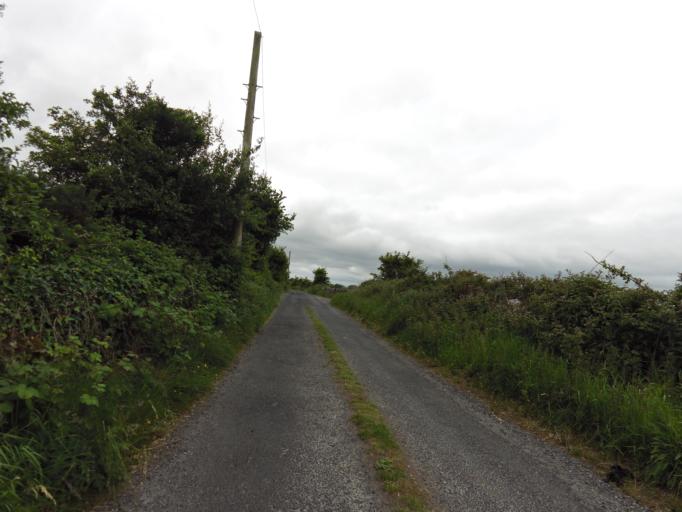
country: IE
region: Connaught
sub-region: County Galway
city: Athenry
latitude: 53.3153
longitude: -8.7389
